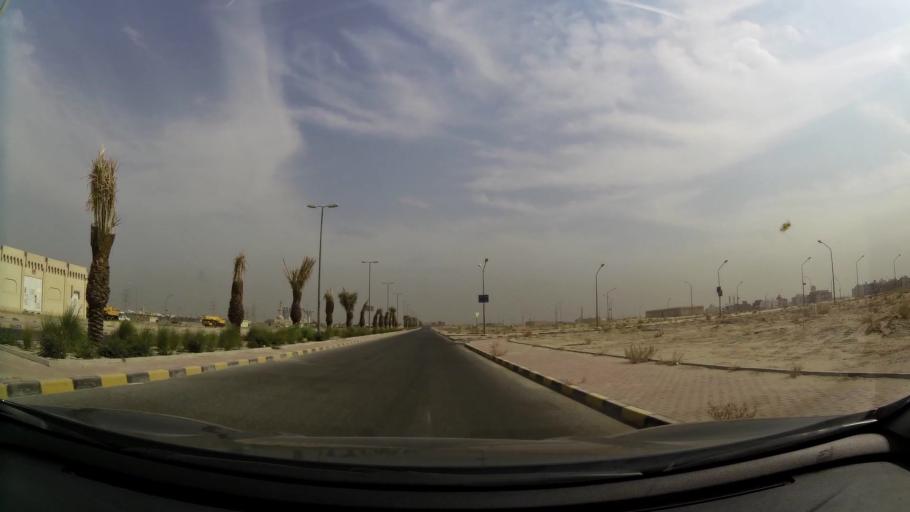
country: KW
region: Al Farwaniyah
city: Janub as Surrah
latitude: 29.2991
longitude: 47.9855
